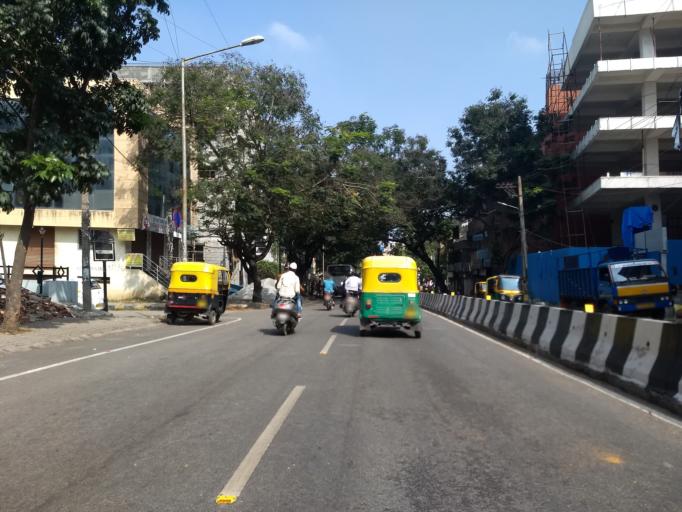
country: IN
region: Karnataka
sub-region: Bangalore Urban
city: Bangalore
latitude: 12.9533
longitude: 77.5799
